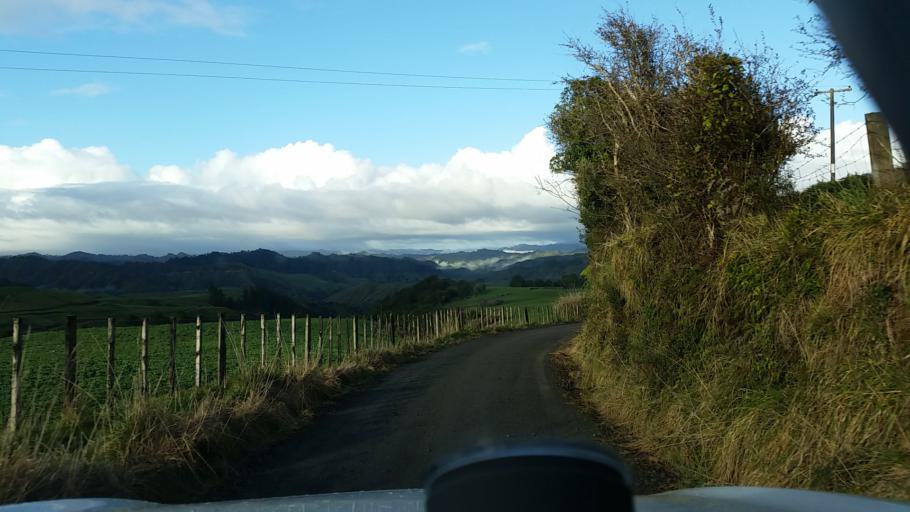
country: NZ
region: Taranaki
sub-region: South Taranaki District
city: Eltham
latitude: -39.4095
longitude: 174.5703
